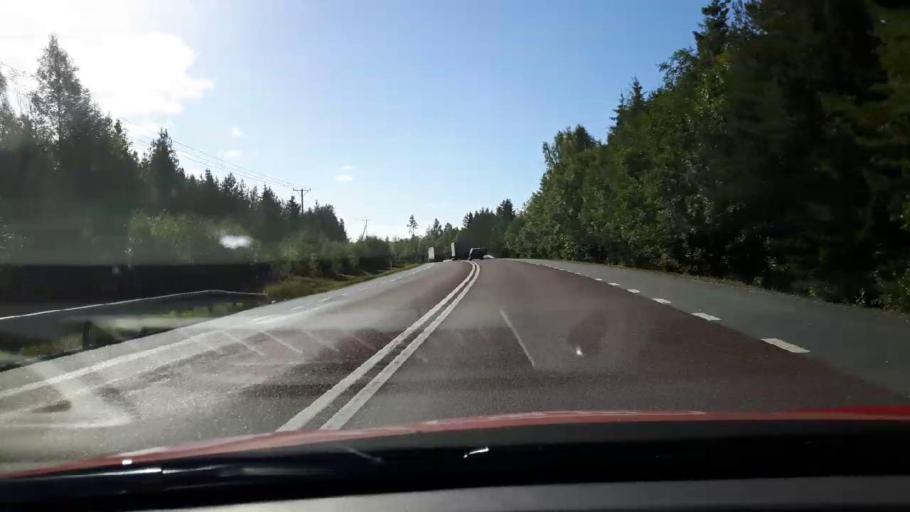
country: SE
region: Jaemtland
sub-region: Braecke Kommun
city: Braecke
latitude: 62.7802
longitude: 15.3864
